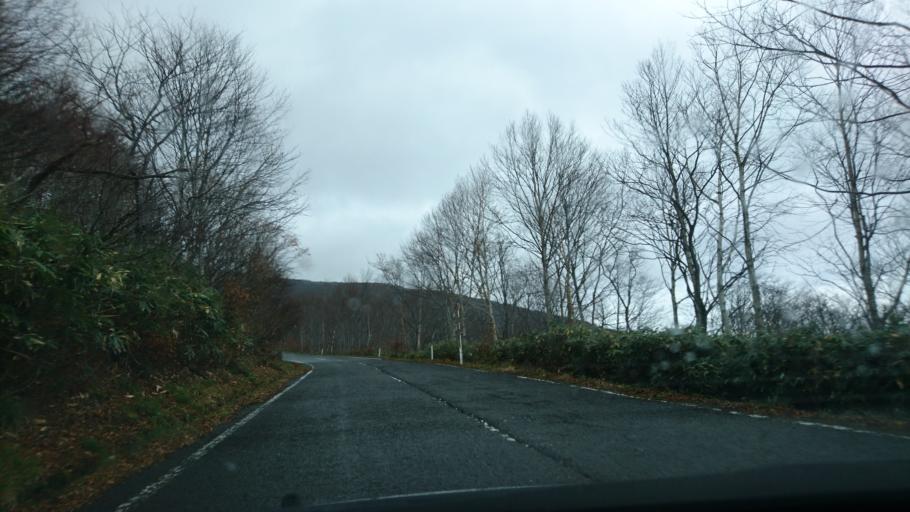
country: JP
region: Iwate
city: Ichinoseki
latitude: 38.9430
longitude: 140.8137
